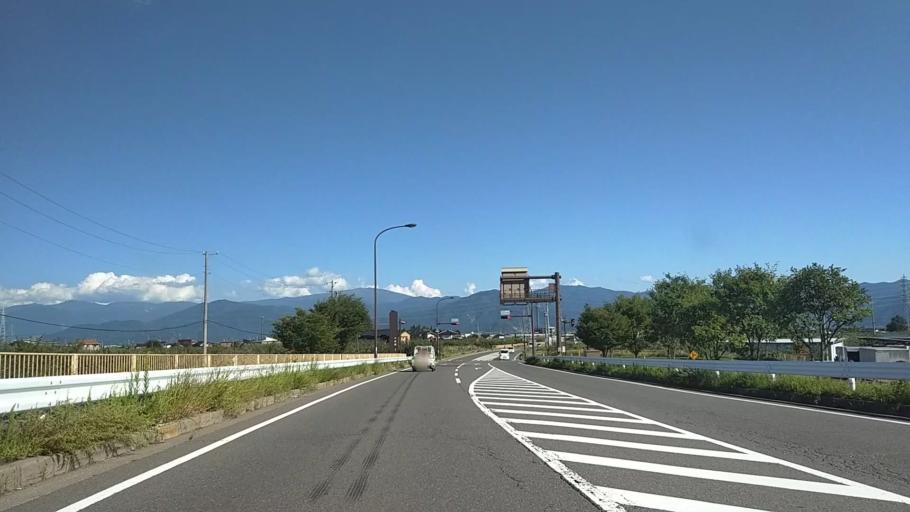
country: JP
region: Nagano
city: Nagano-shi
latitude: 36.6165
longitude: 138.1347
